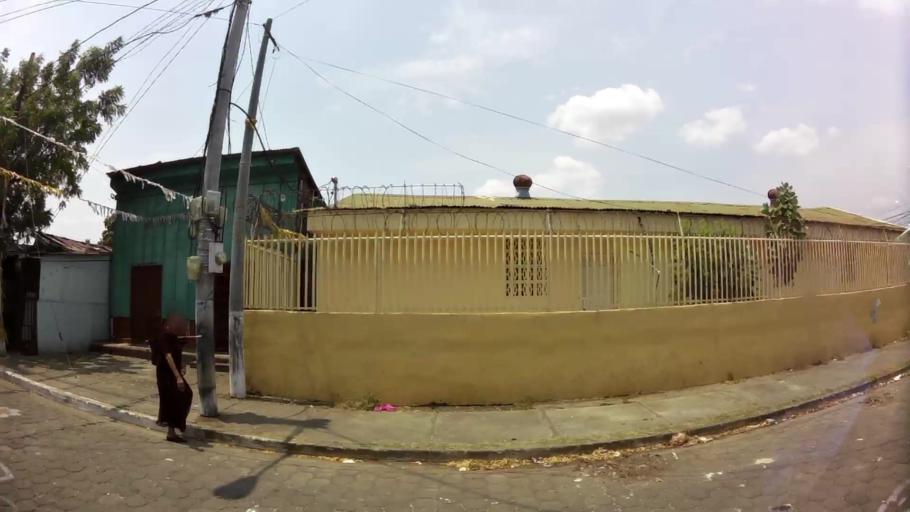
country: NI
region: Managua
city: Ciudad Sandino
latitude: 12.1511
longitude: -86.3027
